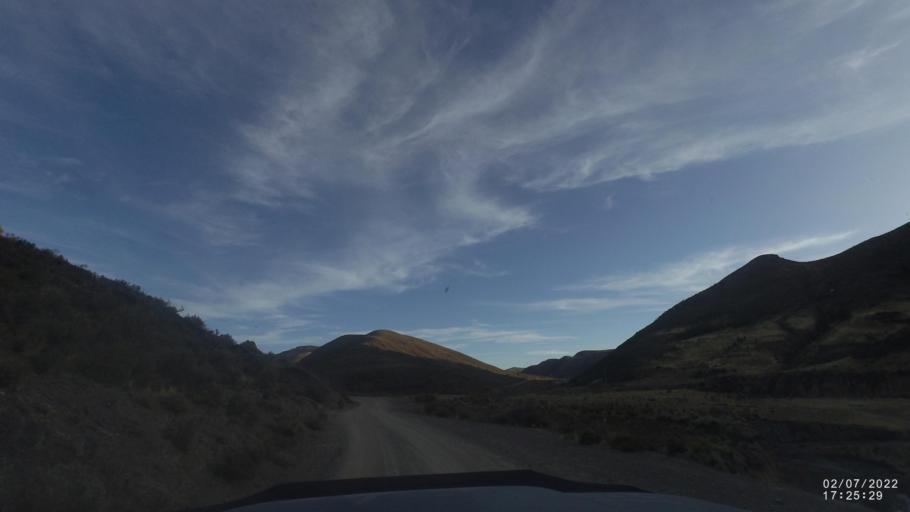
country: BO
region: Cochabamba
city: Irpa Irpa
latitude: -17.8766
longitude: -66.6077
